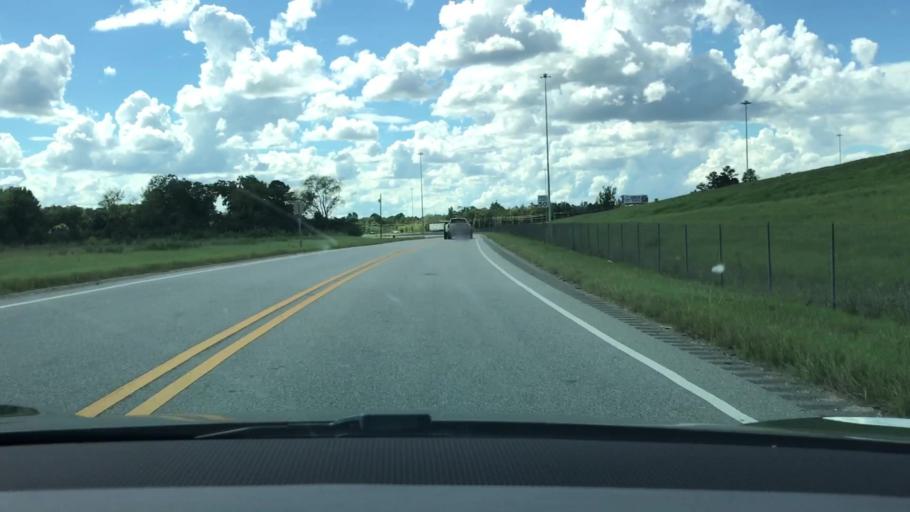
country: US
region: Alabama
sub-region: Montgomery County
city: Pike Road
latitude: 32.3660
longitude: -86.0843
